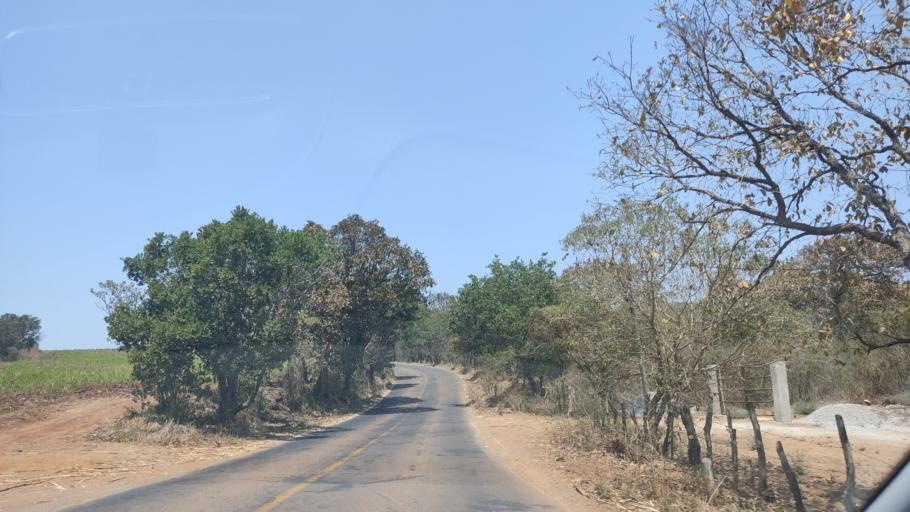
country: MX
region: Nayarit
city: Puga
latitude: 21.5792
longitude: -104.7782
